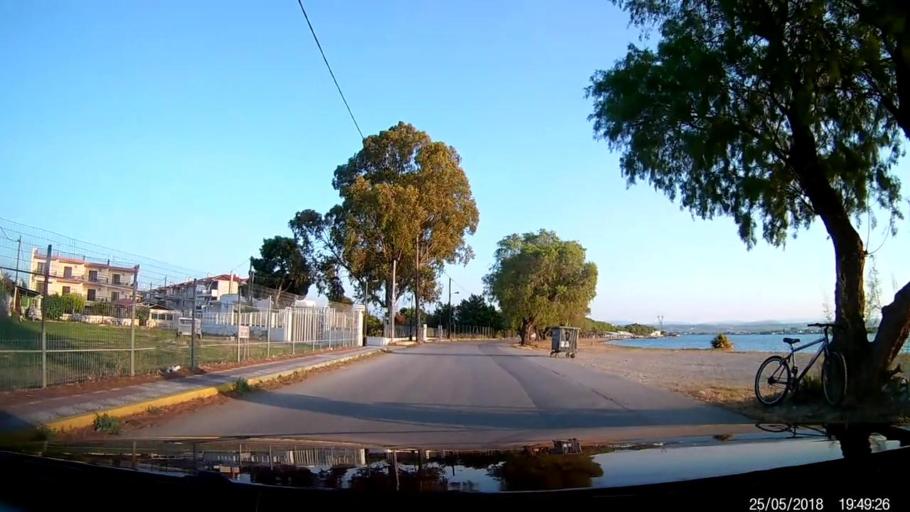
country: GR
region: Central Greece
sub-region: Nomos Evvoias
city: Ayios Nikolaos
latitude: 38.4114
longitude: 23.6411
